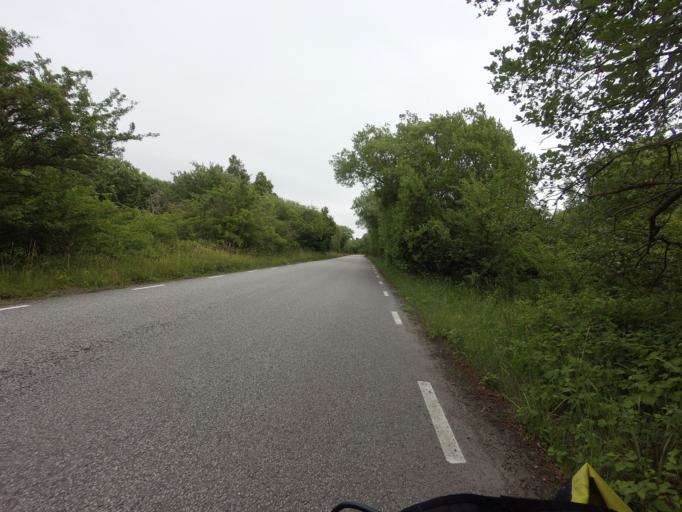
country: SE
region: Skane
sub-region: Malmo
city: Bunkeflostrand
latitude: 55.5245
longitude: 12.9126
